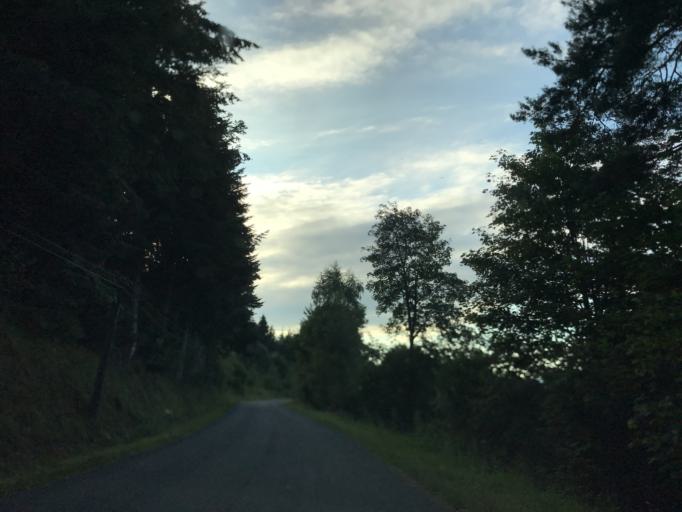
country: FR
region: Rhone-Alpes
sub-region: Departement de la Loire
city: Sail-sous-Couzan
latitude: 45.7431
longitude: 3.8571
